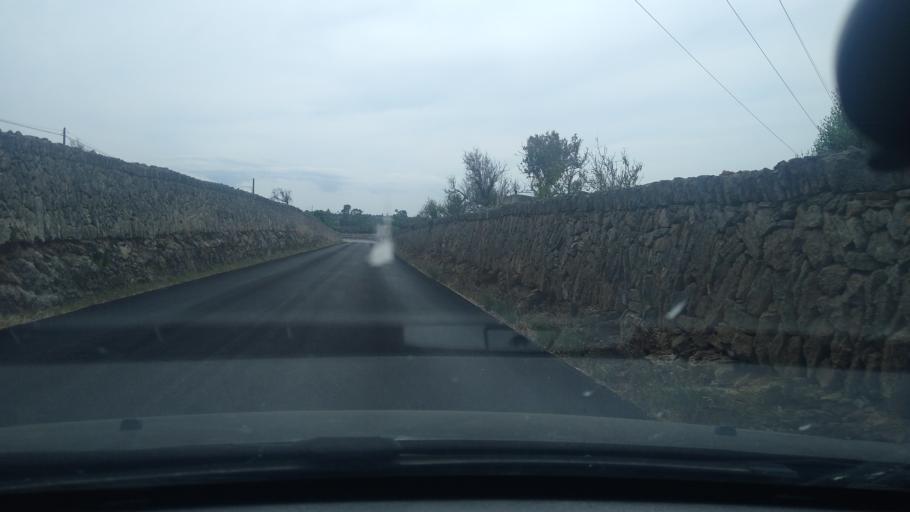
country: ES
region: Balearic Islands
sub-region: Illes Balears
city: Santa Margalida
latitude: 39.7224
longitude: 3.1134
